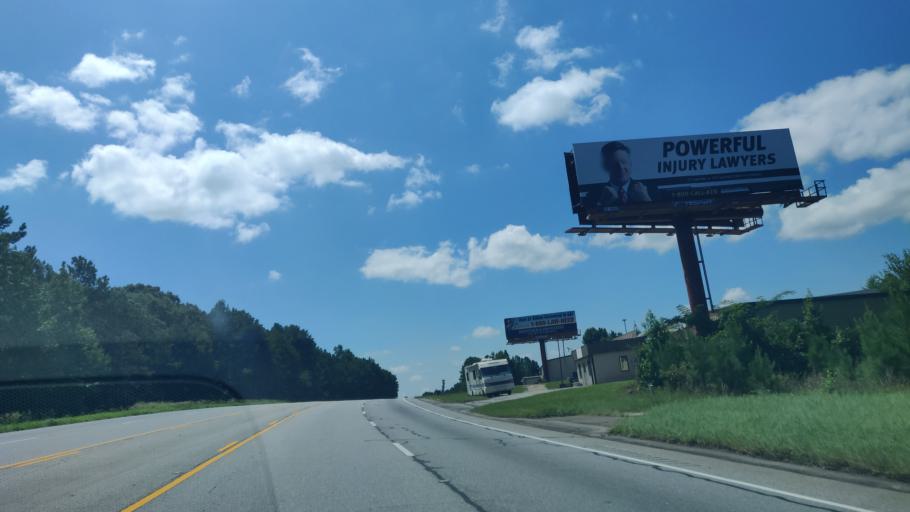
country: US
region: Georgia
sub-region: Chattahoochee County
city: Cusseta
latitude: 32.3072
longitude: -84.7915
